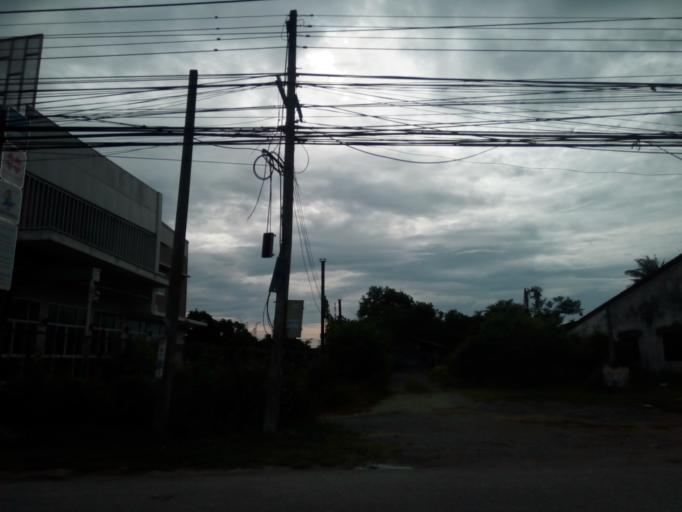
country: TH
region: Phuket
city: Thalang
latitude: 8.0090
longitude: 98.3419
